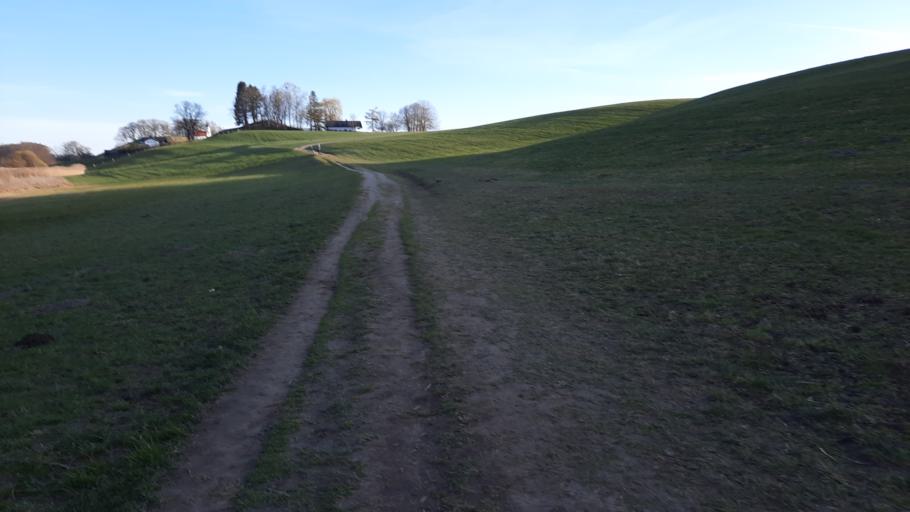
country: DE
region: Bavaria
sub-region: Upper Bavaria
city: Ebersberg
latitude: 48.0854
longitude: 11.9347
